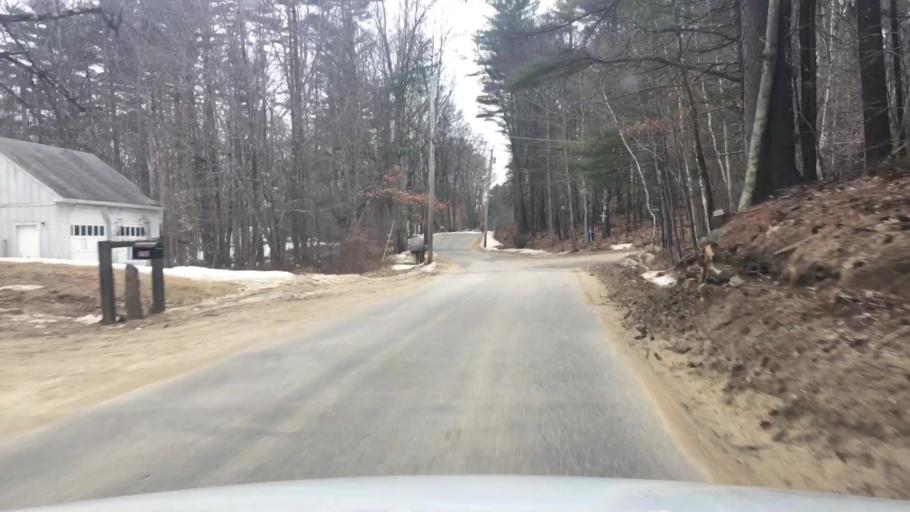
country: US
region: New Hampshire
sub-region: Strafford County
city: Rochester
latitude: 43.3450
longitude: -70.9588
